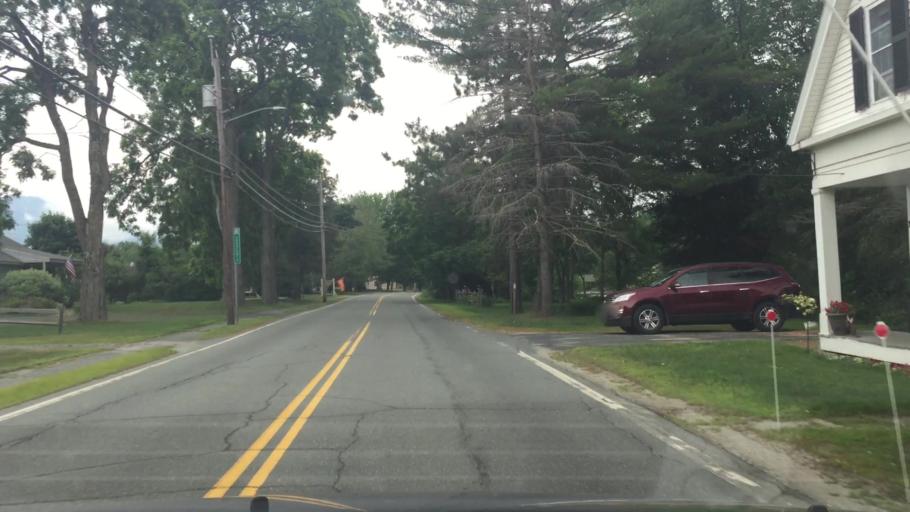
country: US
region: New Hampshire
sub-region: Grafton County
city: Littleton
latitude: 44.2340
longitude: -71.7572
